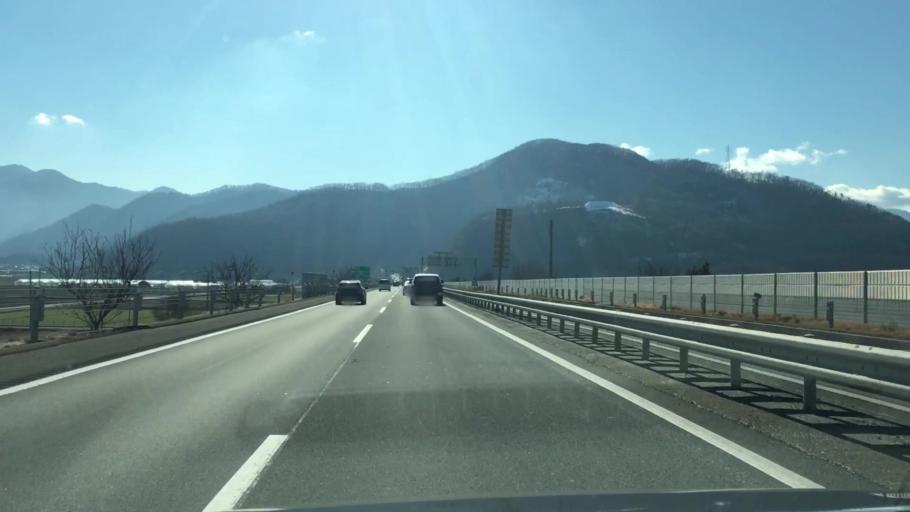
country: JP
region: Nagano
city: Nagano-shi
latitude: 36.5436
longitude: 138.1393
